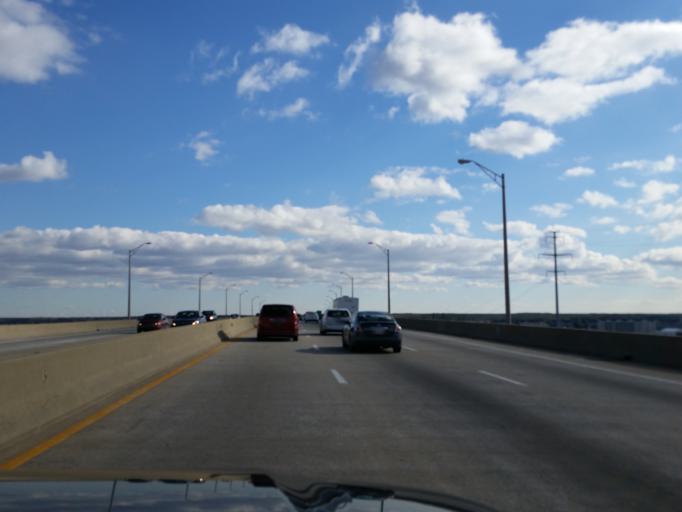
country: US
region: Maryland
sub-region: Queen Anne's County
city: Grasonville
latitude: 38.9711
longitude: -76.2482
